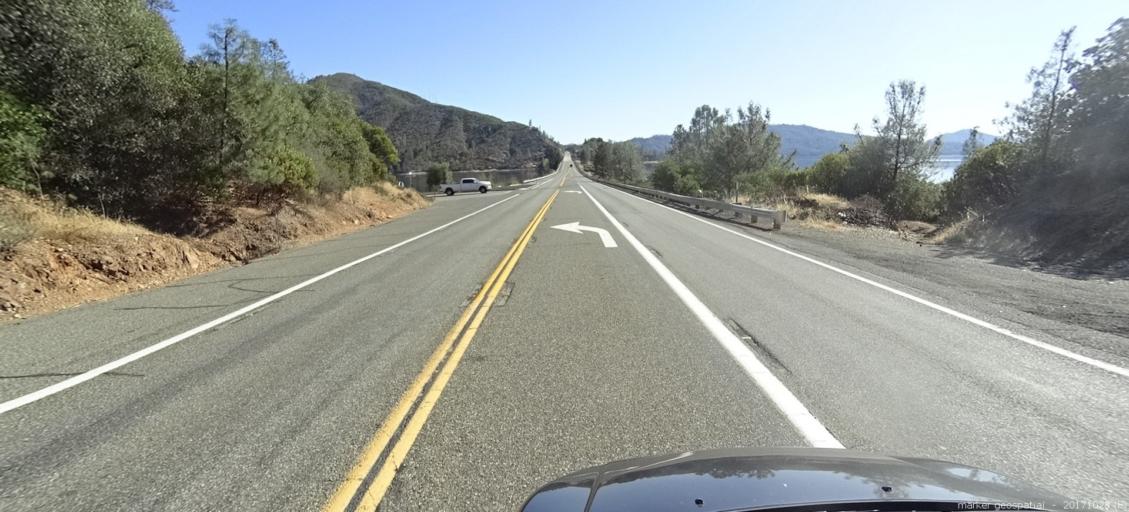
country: US
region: California
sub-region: Shasta County
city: Shasta
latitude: 40.6346
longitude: -122.5622
